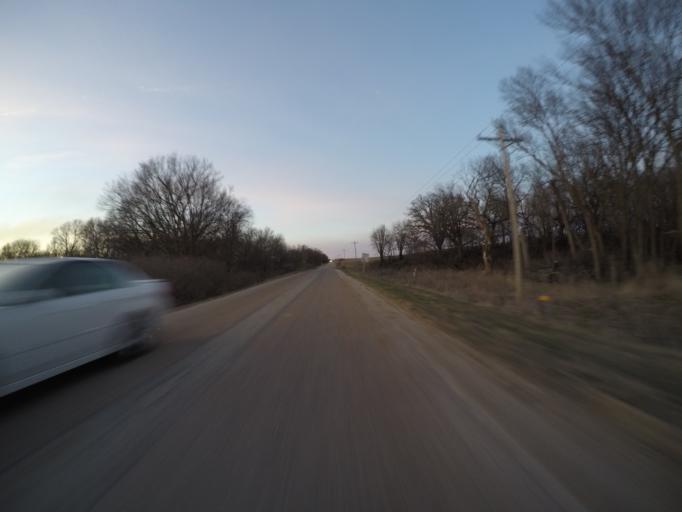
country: US
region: Kansas
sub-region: Washington County
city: Washington
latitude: 39.6870
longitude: -96.9754
